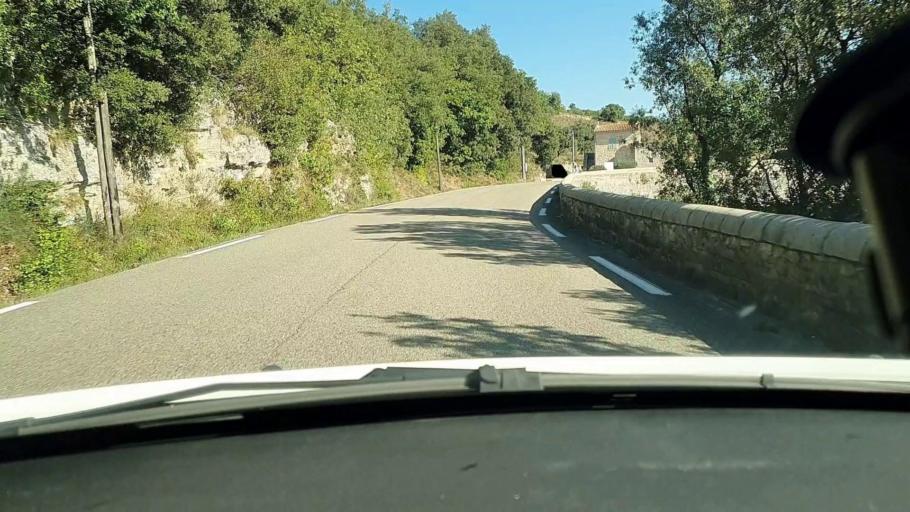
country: FR
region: Languedoc-Roussillon
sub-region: Departement du Gard
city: Goudargues
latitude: 44.2729
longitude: 4.4339
